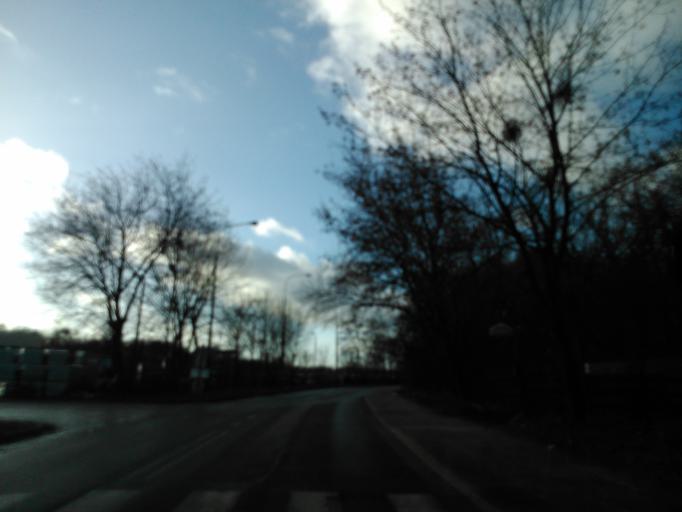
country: PL
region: Kujawsko-Pomorskie
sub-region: Torun
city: Torun
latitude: 53.0008
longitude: 18.6125
